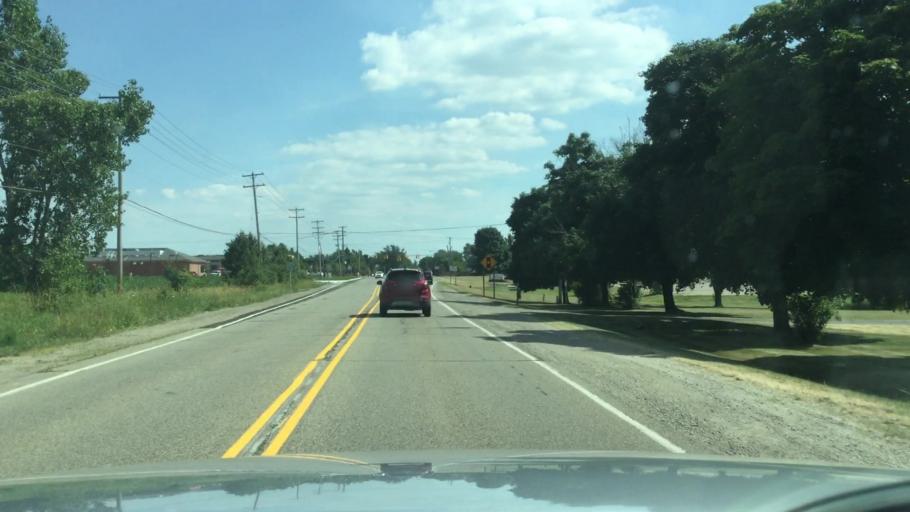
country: US
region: Michigan
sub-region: Genesee County
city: Grand Blanc
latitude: 42.9336
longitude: -83.5971
